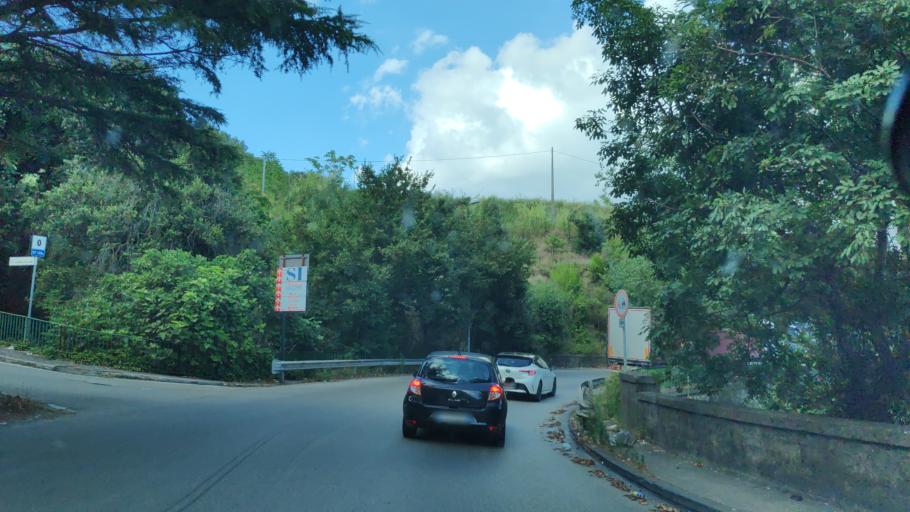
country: IT
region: Campania
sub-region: Provincia di Salerno
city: Capezzano Inferiore
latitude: 40.6847
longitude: 14.7585
